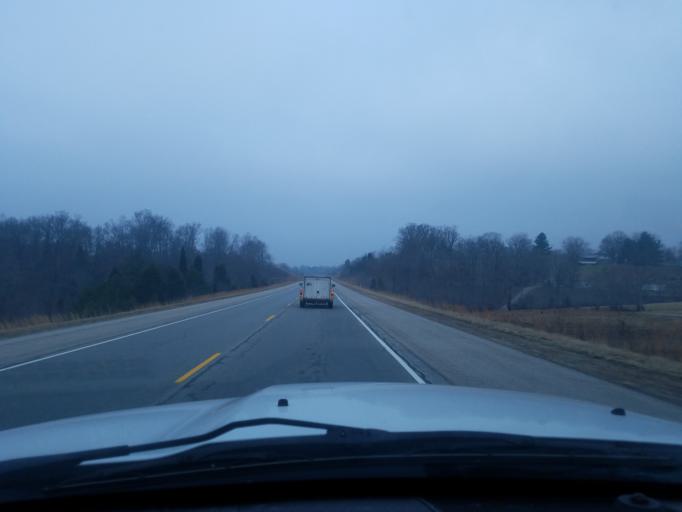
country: US
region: Indiana
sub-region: Perry County
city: Tell City
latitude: 38.0479
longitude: -86.6430
